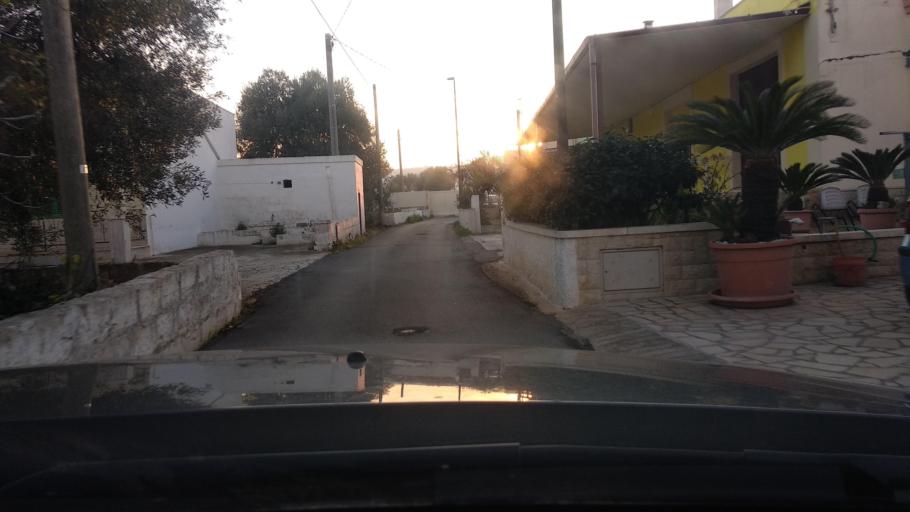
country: IT
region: Apulia
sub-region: Provincia di Brindisi
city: Fasano
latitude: 40.8824
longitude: 17.3339
